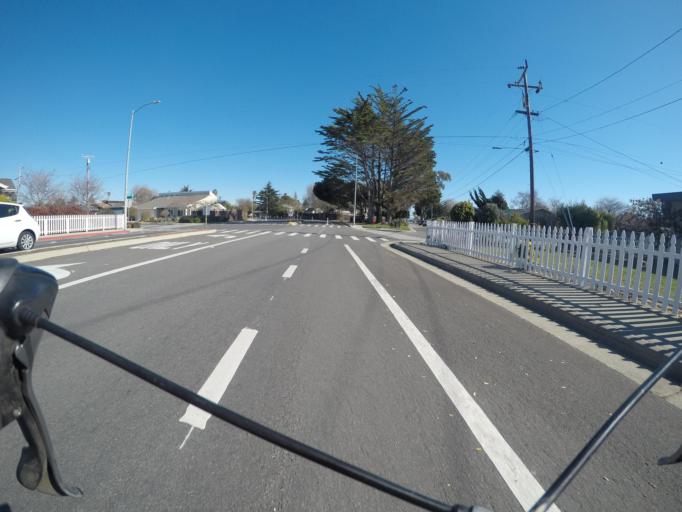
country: US
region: California
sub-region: Santa Cruz County
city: Santa Cruz
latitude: 36.9579
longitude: -122.0308
